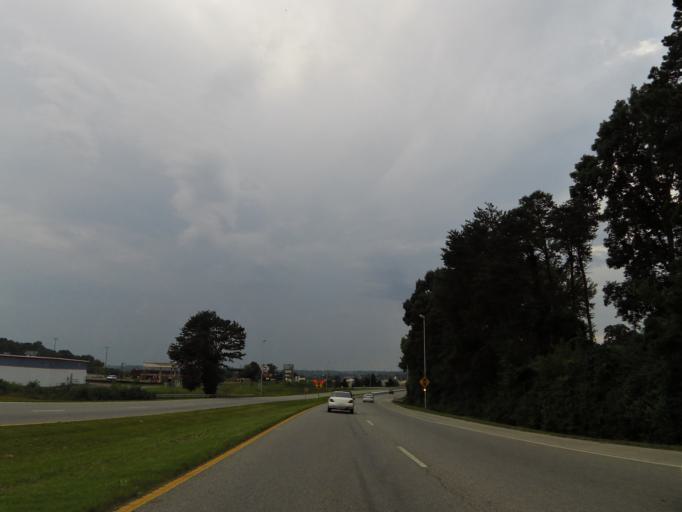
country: US
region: Tennessee
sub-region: Blount County
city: Maryville
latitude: 35.7419
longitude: -83.9906
